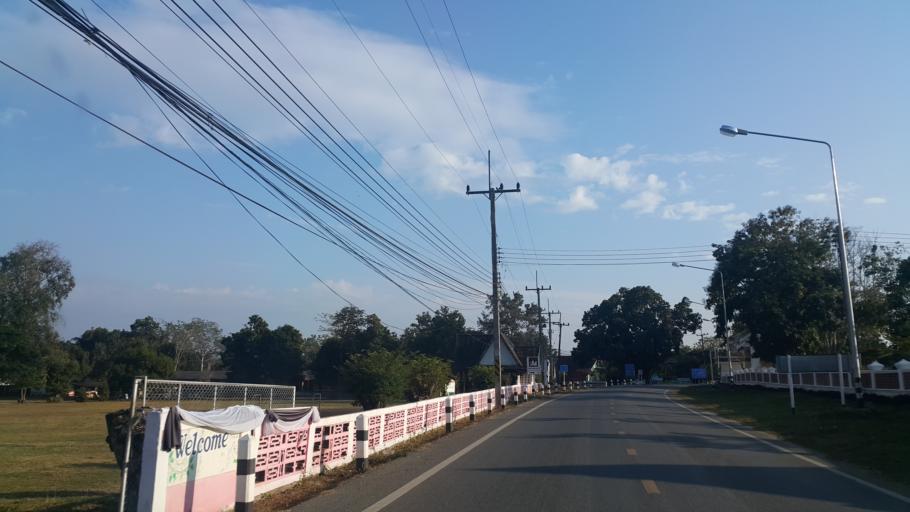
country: TH
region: Lampang
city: Soem Ngam
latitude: 18.0972
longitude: 99.3409
